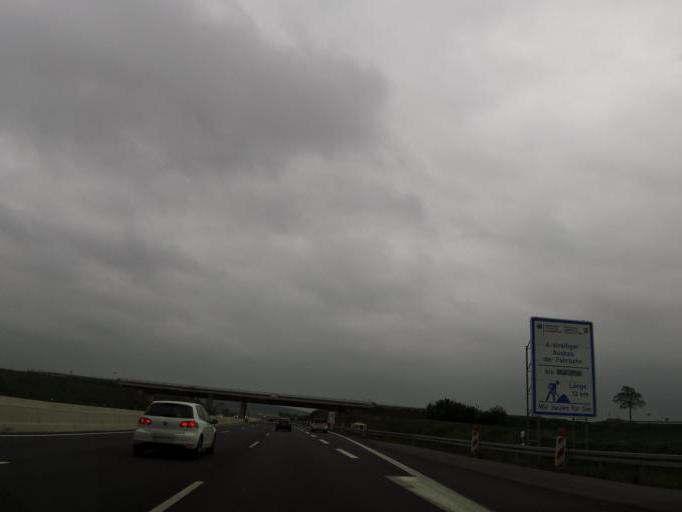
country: DE
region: Lower Saxony
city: Bockenem
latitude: 52.0007
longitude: 10.1566
